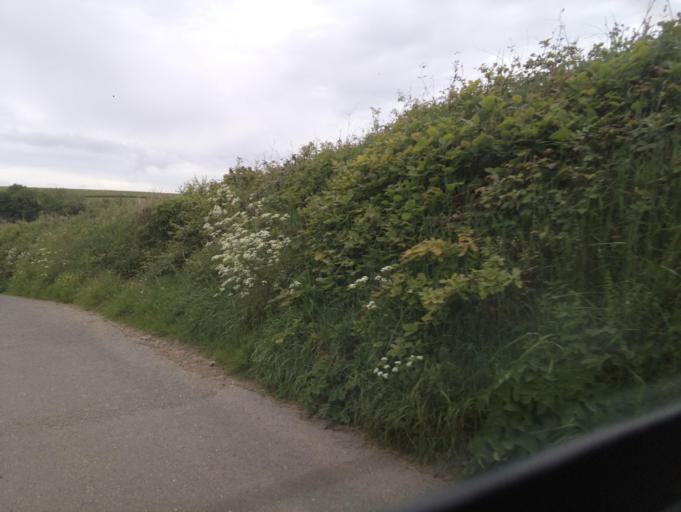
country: GB
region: England
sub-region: Devon
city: Dartmouth
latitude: 50.3352
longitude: -3.6486
